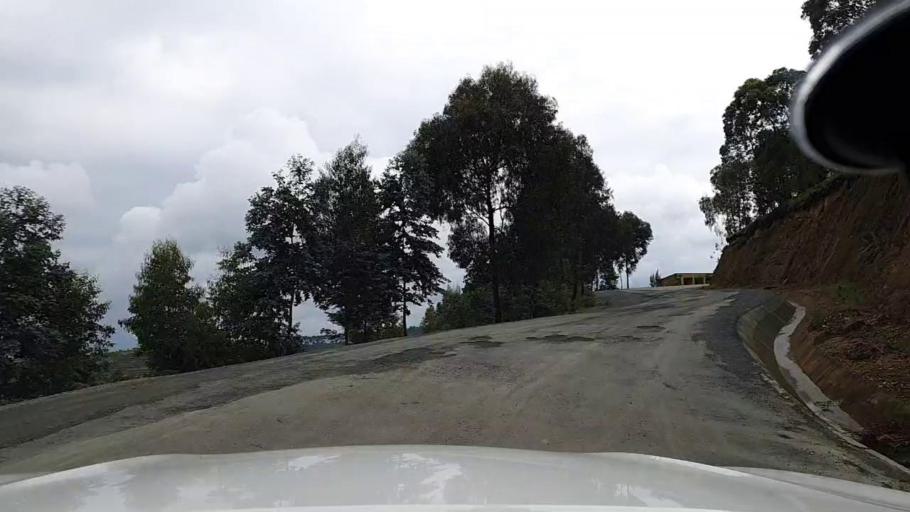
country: RW
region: Western Province
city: Kibuye
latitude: -2.0693
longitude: 29.5426
